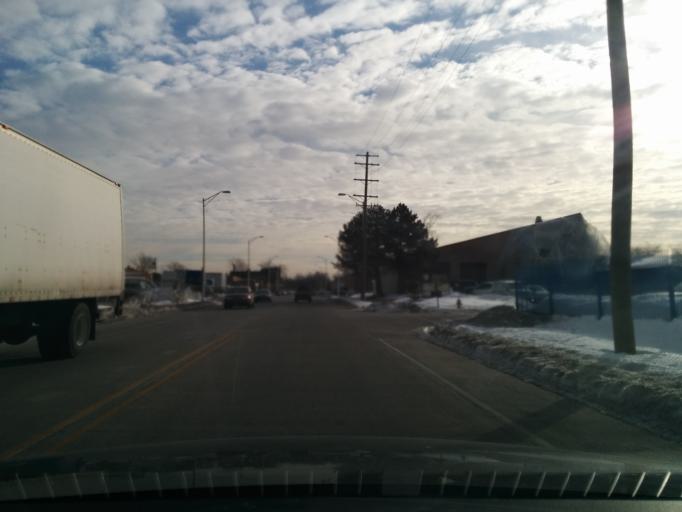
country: US
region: Illinois
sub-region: Cook County
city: Maywood
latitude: 41.8880
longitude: -87.8433
